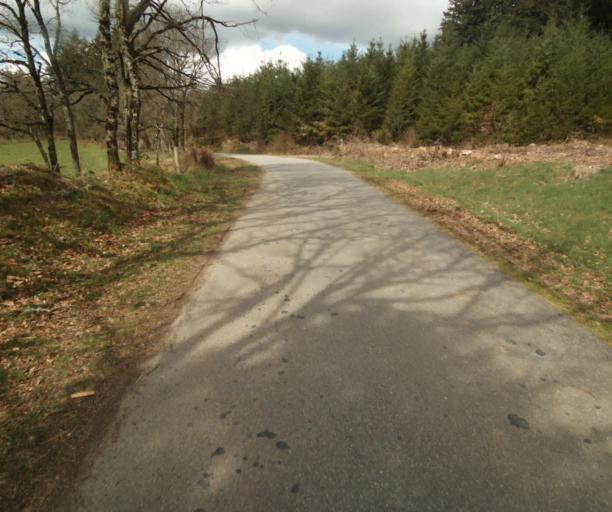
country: FR
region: Limousin
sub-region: Departement de la Correze
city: Correze
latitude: 45.3931
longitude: 1.9071
